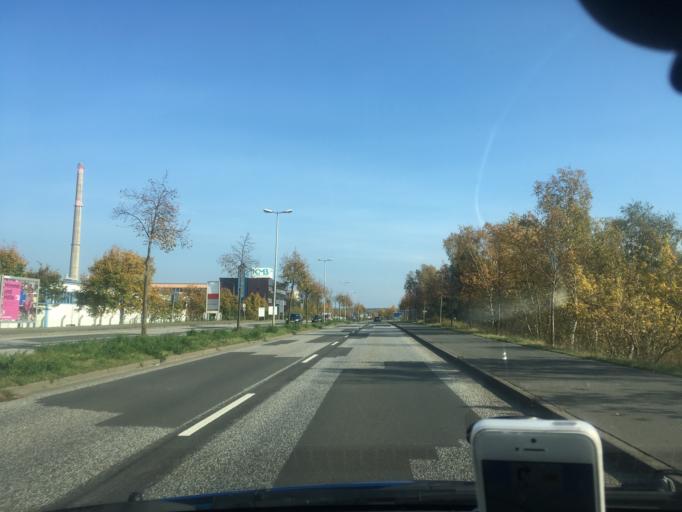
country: DE
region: Mecklenburg-Vorpommern
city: Feldstadt
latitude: 53.5721
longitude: 11.3909
